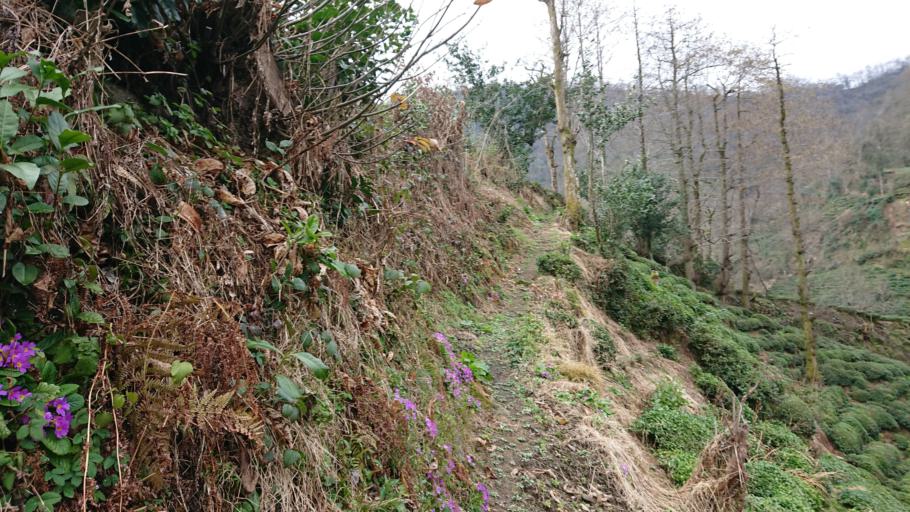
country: TR
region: Rize
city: Rize
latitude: 40.9805
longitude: 40.4945
